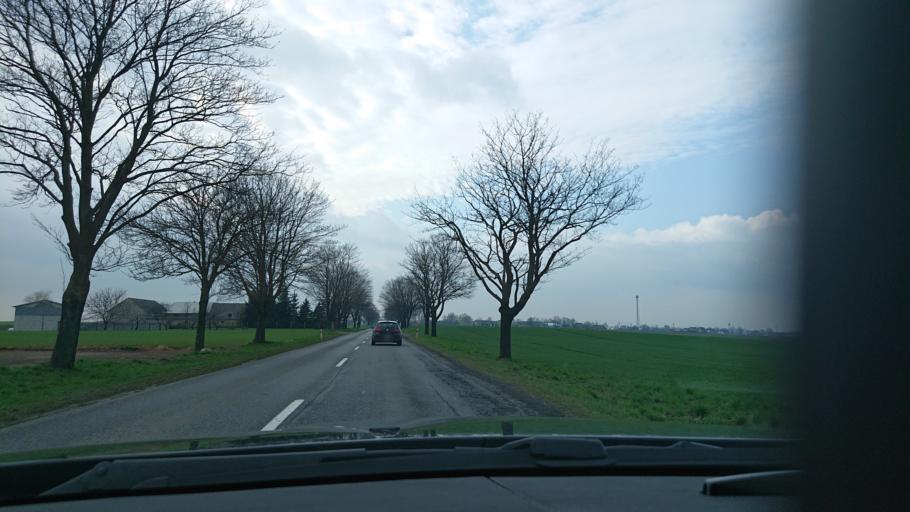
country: PL
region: Greater Poland Voivodeship
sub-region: Powiat gnieznienski
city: Gniezno
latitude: 52.5570
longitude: 17.5355
